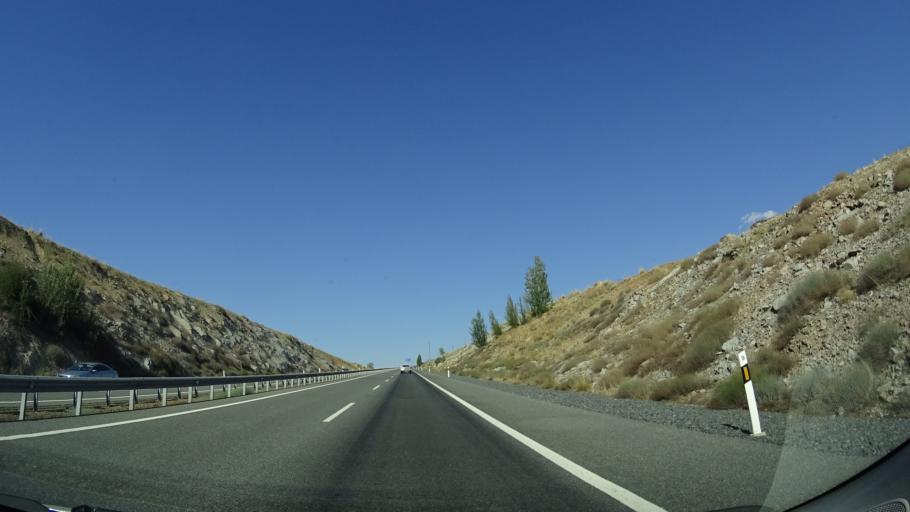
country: ES
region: Castille and Leon
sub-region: Provincia de Avila
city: Avila
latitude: 40.6734
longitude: -4.7014
